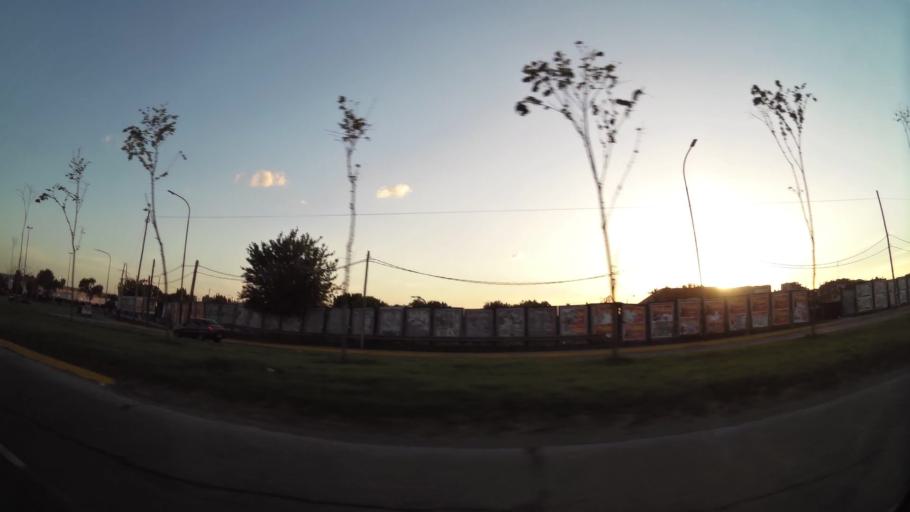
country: AR
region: Buenos Aires F.D.
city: Villa Lugano
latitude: -34.6724
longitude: -58.4601
